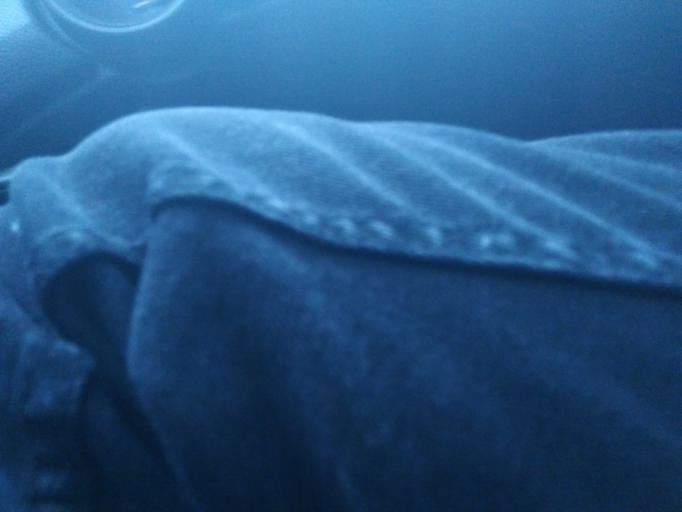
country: BY
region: Minsk
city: Haradzyeya
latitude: 53.3385
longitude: 26.5209
